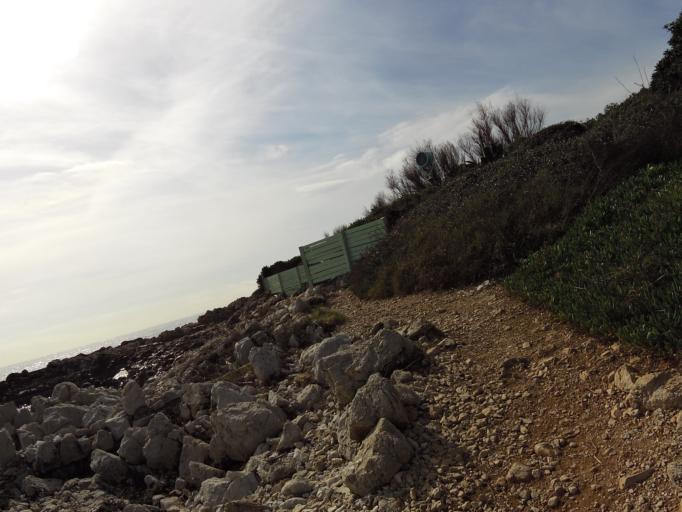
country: FR
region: Provence-Alpes-Cote d'Azur
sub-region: Departement des Alpes-Maritimes
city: Antibes
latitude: 43.5465
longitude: 7.1377
